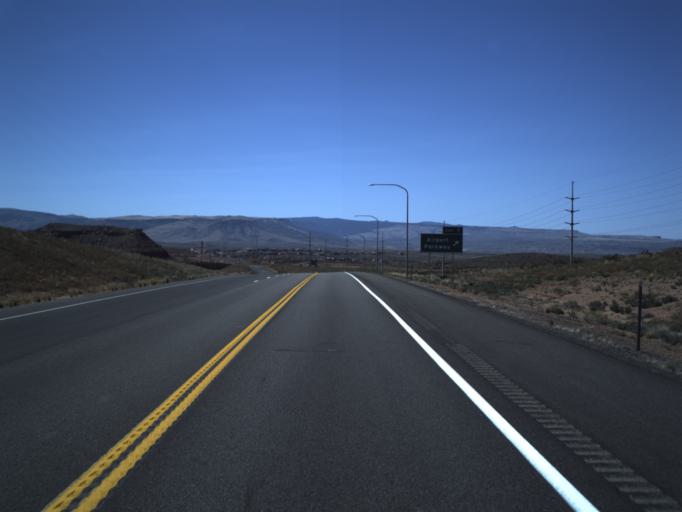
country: US
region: Utah
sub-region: Washington County
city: Washington
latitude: 37.0200
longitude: -113.4897
